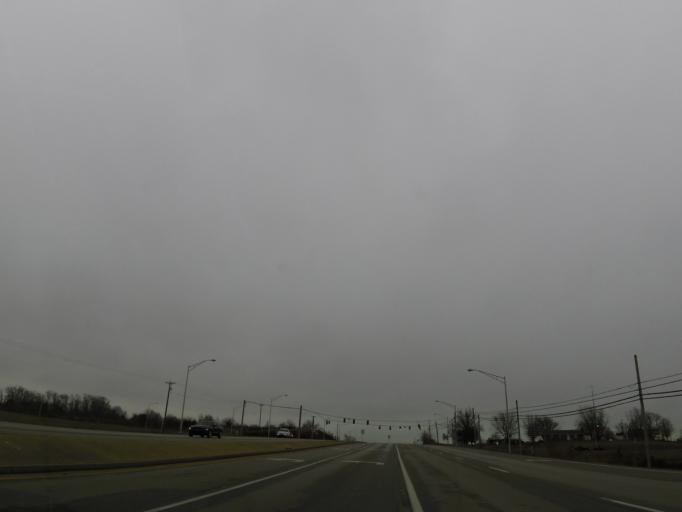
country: US
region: Kentucky
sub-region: Mercer County
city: Harrodsburg
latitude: 37.7881
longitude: -84.8466
